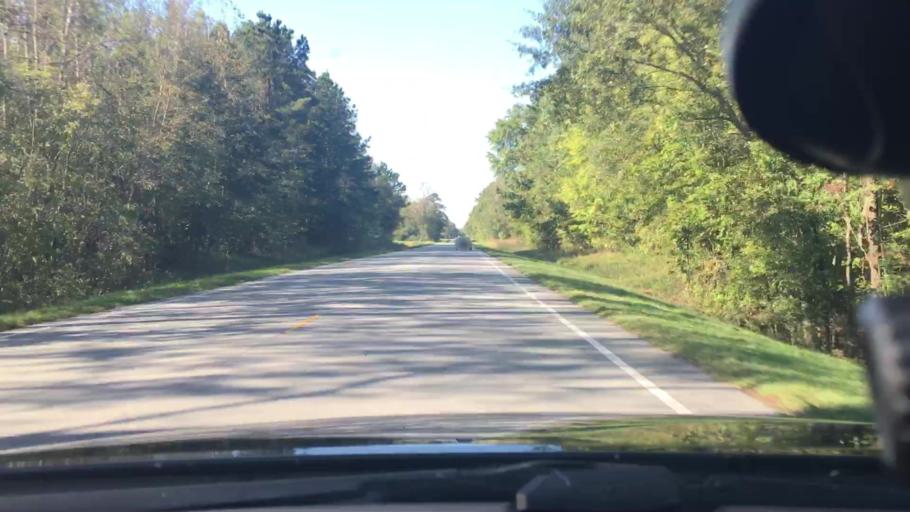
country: US
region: North Carolina
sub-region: Craven County
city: Vanceboro
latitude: 35.3037
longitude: -77.1341
